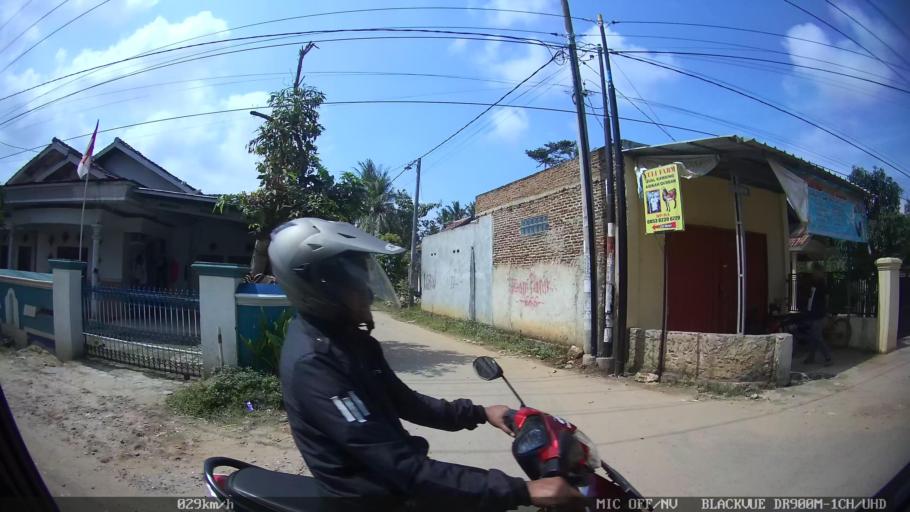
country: ID
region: Lampung
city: Kedaton
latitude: -5.3421
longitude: 105.2873
